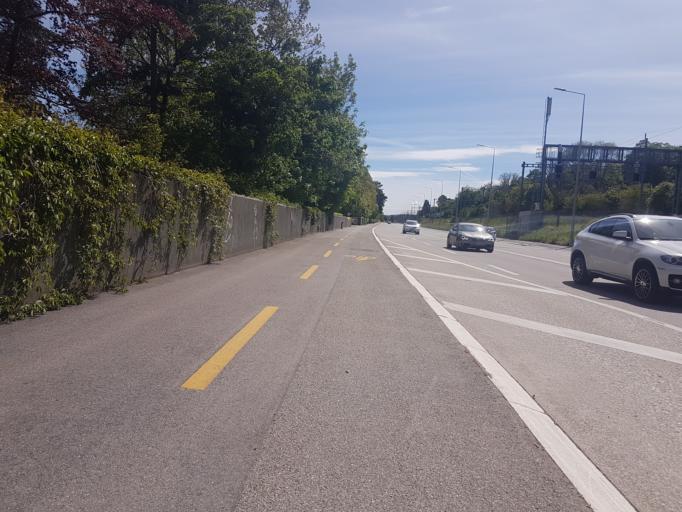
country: CH
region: Geneva
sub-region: Geneva
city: Versoix
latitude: 46.2711
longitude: 6.1661
